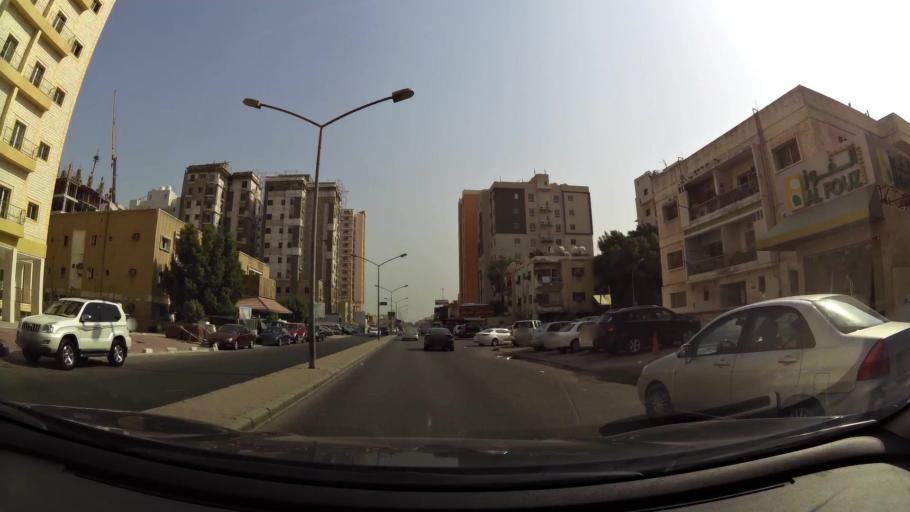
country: KW
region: Muhafazat Hawalli
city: Ar Rumaythiyah
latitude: 29.3232
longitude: 48.0596
